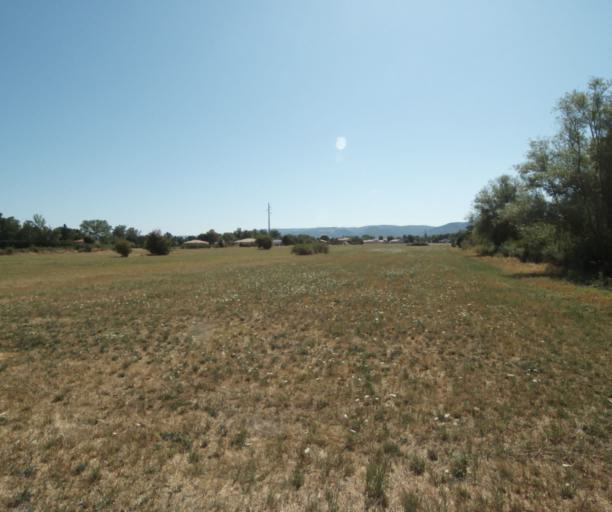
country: FR
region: Midi-Pyrenees
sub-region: Departement de la Haute-Garonne
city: Revel
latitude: 43.4695
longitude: 1.9937
